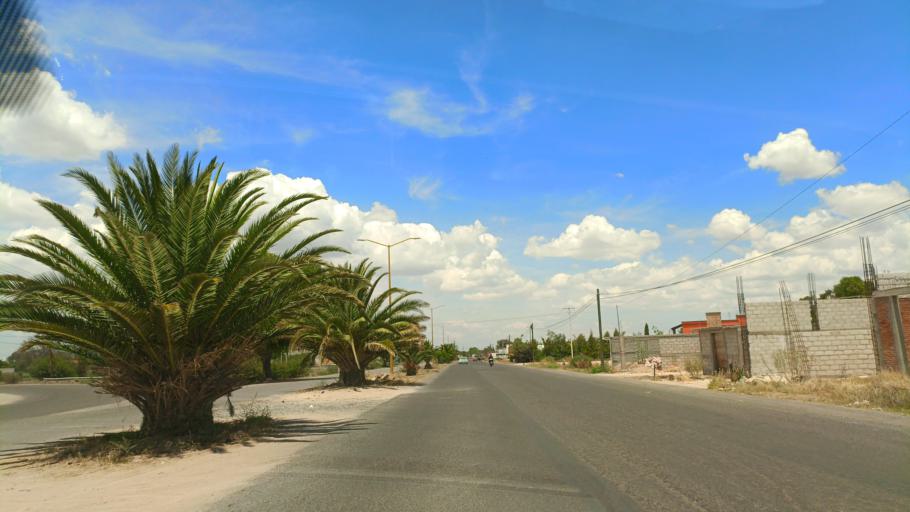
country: MX
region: Guanajuato
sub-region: San Luis de la Paz
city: San Ignacio
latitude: 21.2889
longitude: -100.5526
